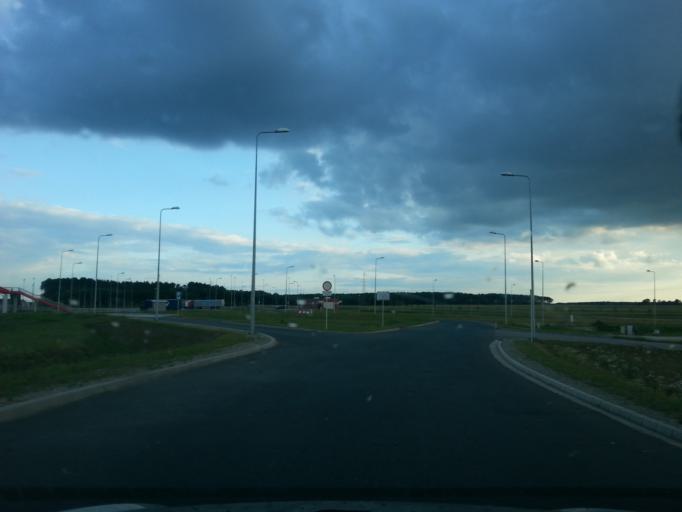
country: PL
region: Lodz Voivodeship
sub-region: Powiat sieradzki
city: Sieradz
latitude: 51.5297
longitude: 18.6955
